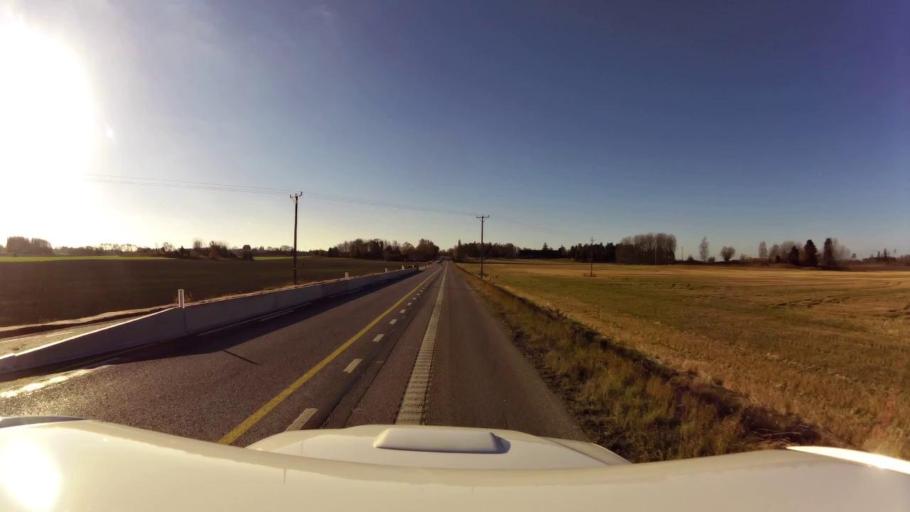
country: SE
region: OEstergoetland
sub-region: Linkopings Kommun
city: Linghem
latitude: 58.4347
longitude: 15.7343
